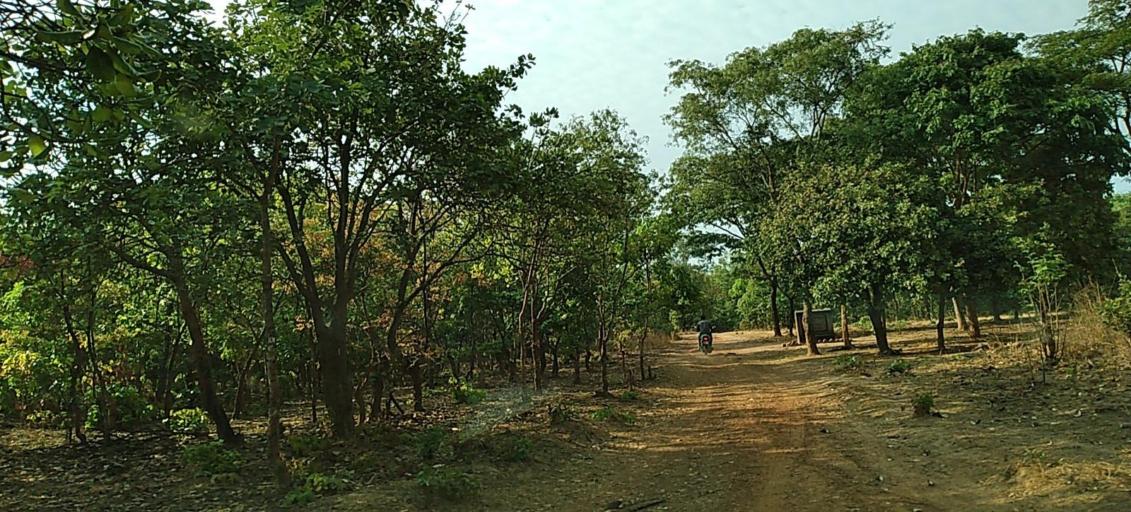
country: ZM
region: Copperbelt
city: Kalulushi
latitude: -12.9629
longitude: 27.7005
